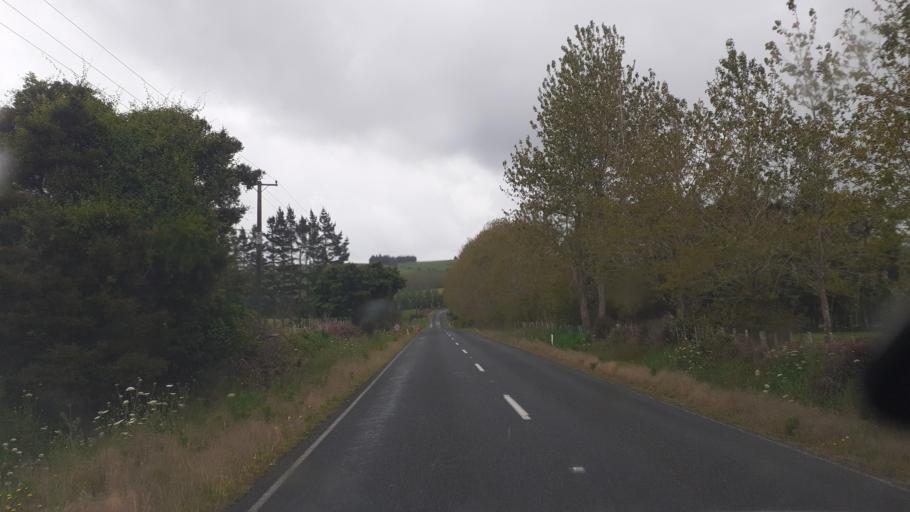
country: NZ
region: Northland
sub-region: Far North District
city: Waimate North
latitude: -35.2720
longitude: 173.8255
